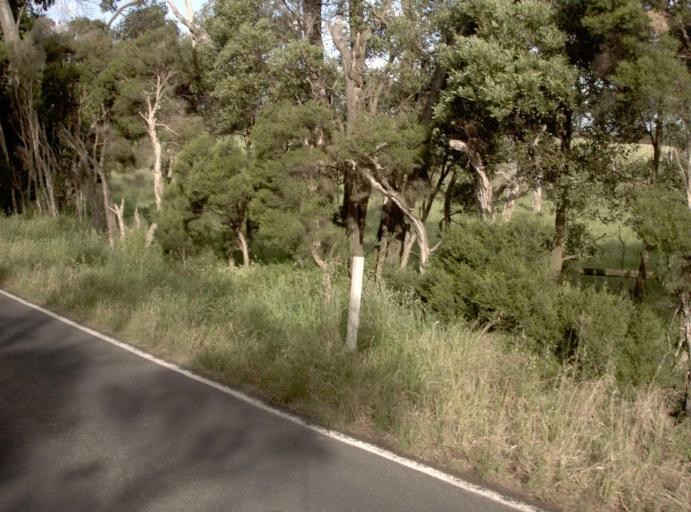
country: AU
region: Victoria
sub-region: Baw Baw
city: Warragul
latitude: -38.4895
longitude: 145.9322
